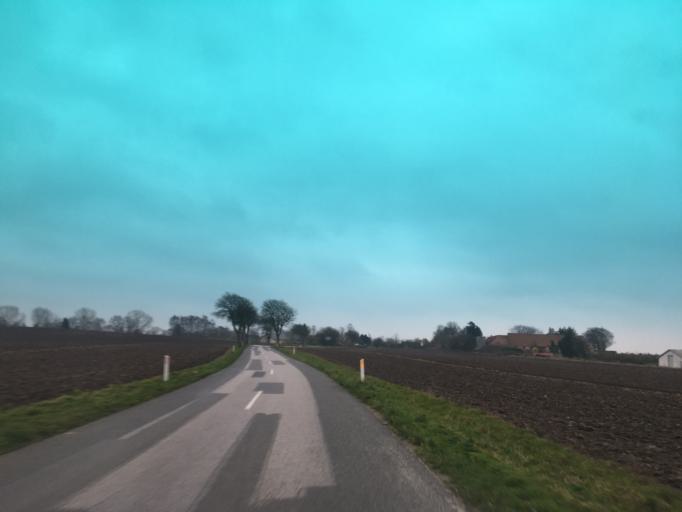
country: DK
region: Zealand
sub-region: Slagelse Kommune
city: Skaelskor
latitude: 55.2428
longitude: 11.4235
